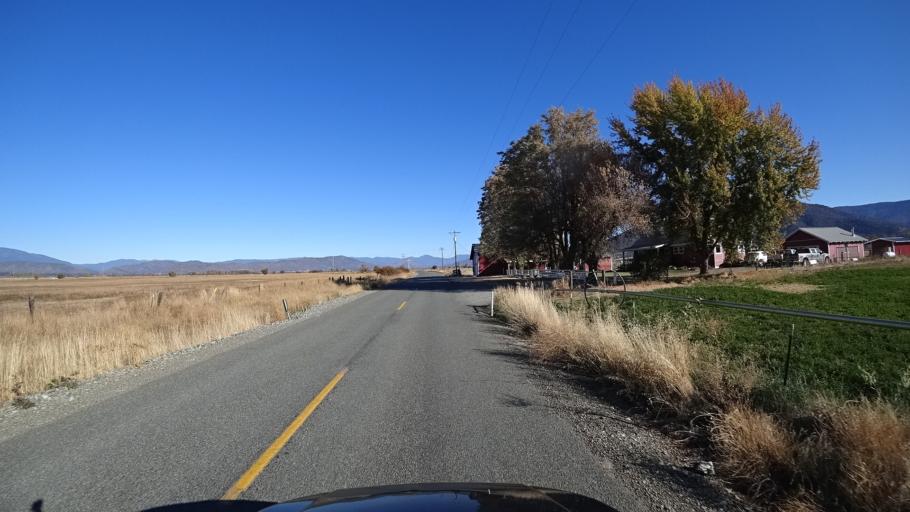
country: US
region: California
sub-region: Siskiyou County
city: Yreka
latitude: 41.4973
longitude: -122.8591
